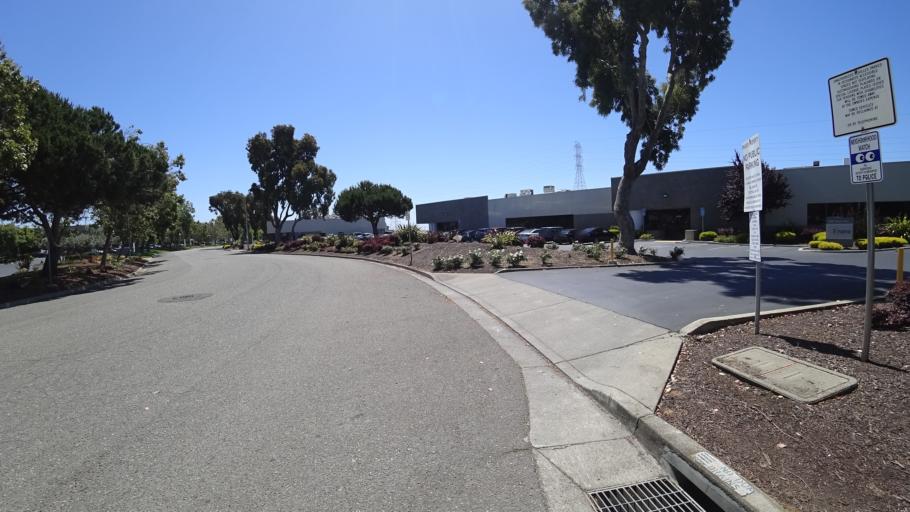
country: US
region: California
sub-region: Alameda County
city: San Lorenzo
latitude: 37.6236
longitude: -122.1264
